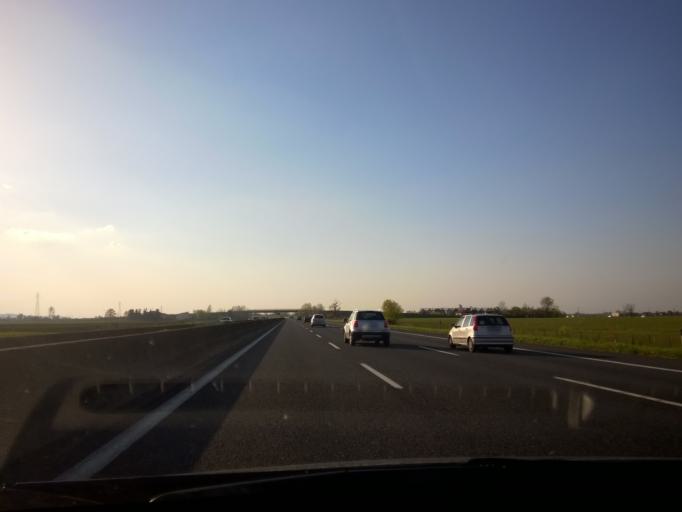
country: IT
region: Emilia-Romagna
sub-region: Provincia di Bologna
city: Osteria Grande
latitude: 44.4515
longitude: 11.5399
